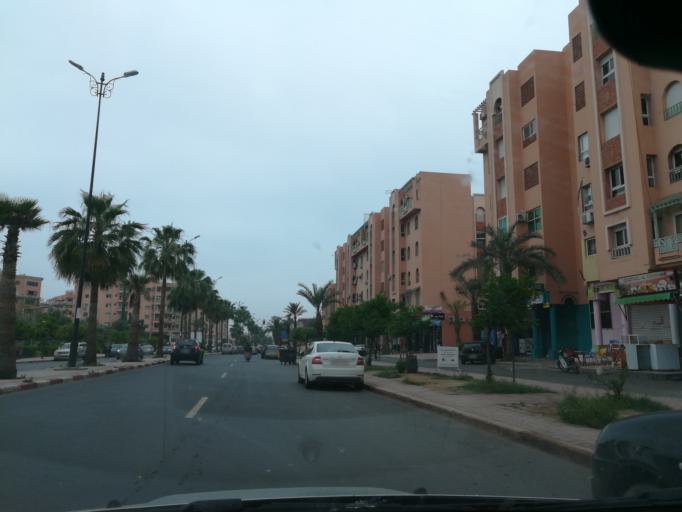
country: MA
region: Marrakech-Tensift-Al Haouz
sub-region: Marrakech
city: Marrakesh
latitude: 31.6633
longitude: -8.0085
